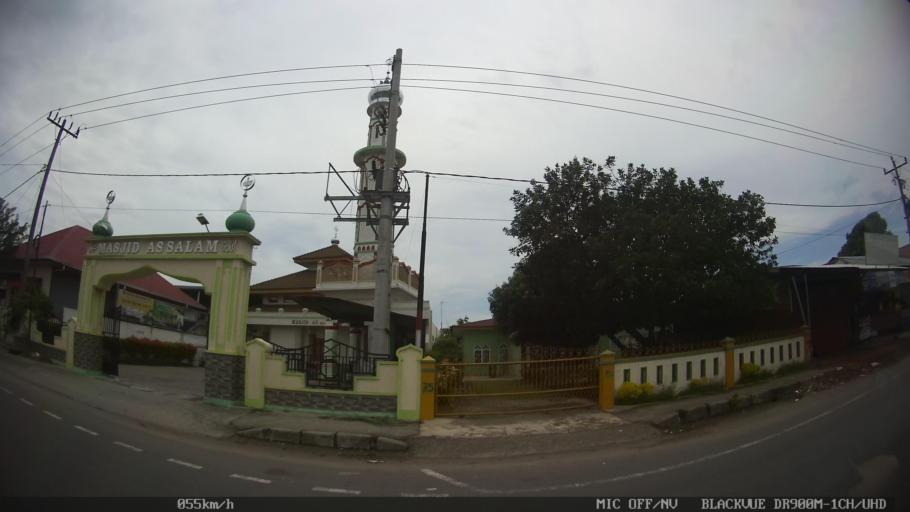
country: ID
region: North Sumatra
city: Sunggal
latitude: 3.6082
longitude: 98.5756
